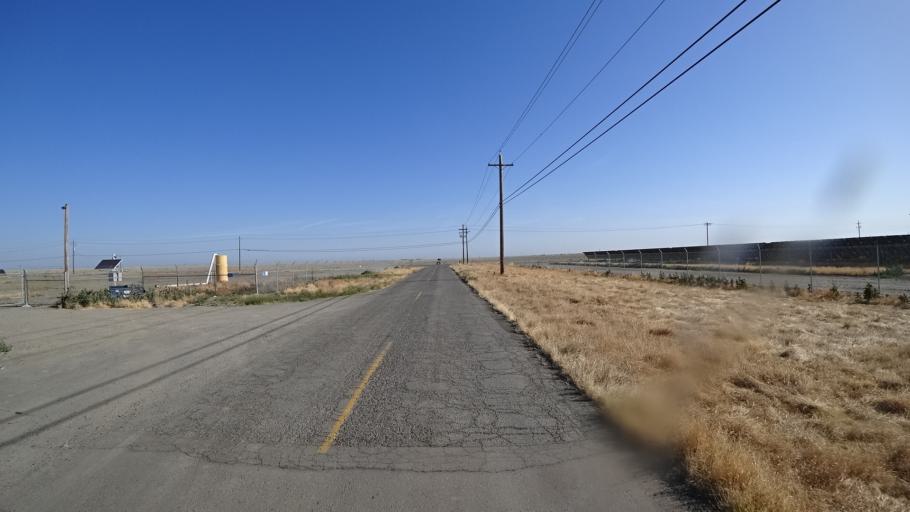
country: US
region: California
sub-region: Kings County
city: Corcoran
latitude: 36.1368
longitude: -119.5543
